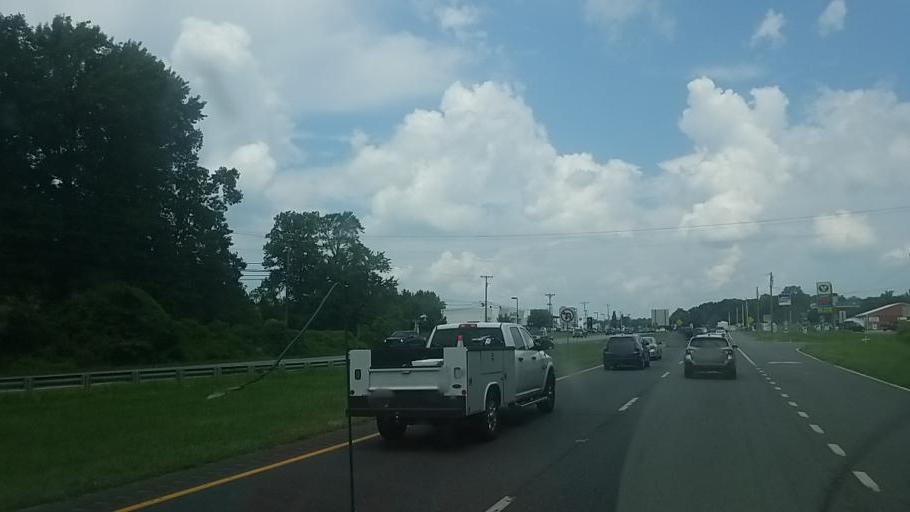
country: US
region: Delaware
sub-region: Sussex County
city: Milford
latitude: 38.9440
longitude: -75.4267
